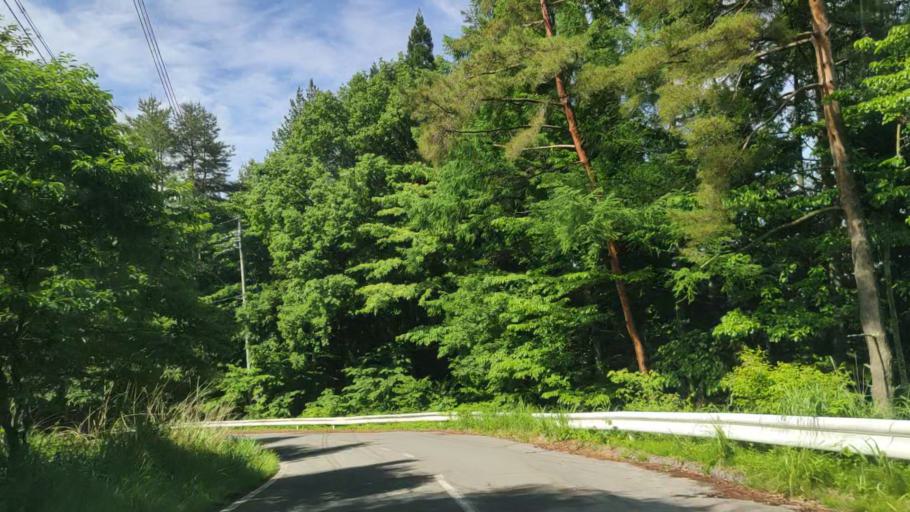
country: JP
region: Nagano
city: Suwa
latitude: 36.0728
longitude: 138.1374
